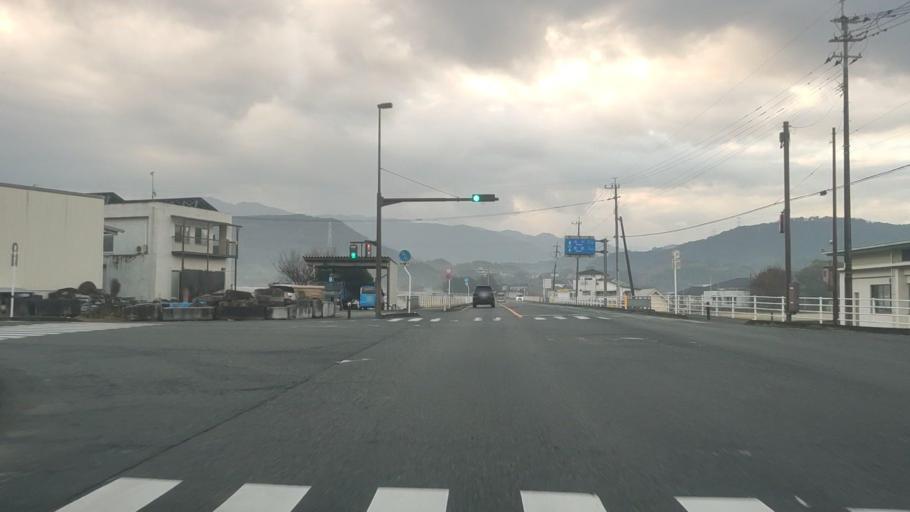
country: JP
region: Kumamoto
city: Matsubase
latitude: 32.6480
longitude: 130.8114
